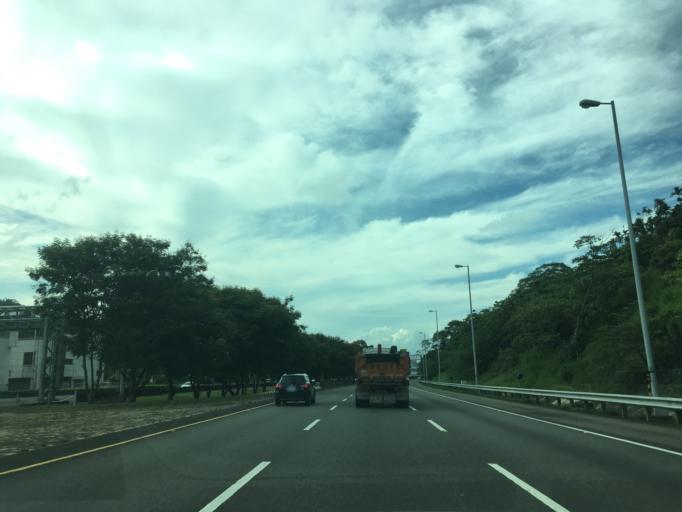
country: TW
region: Taiwan
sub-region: Chiayi
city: Jiayi Shi
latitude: 23.4877
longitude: 120.4963
